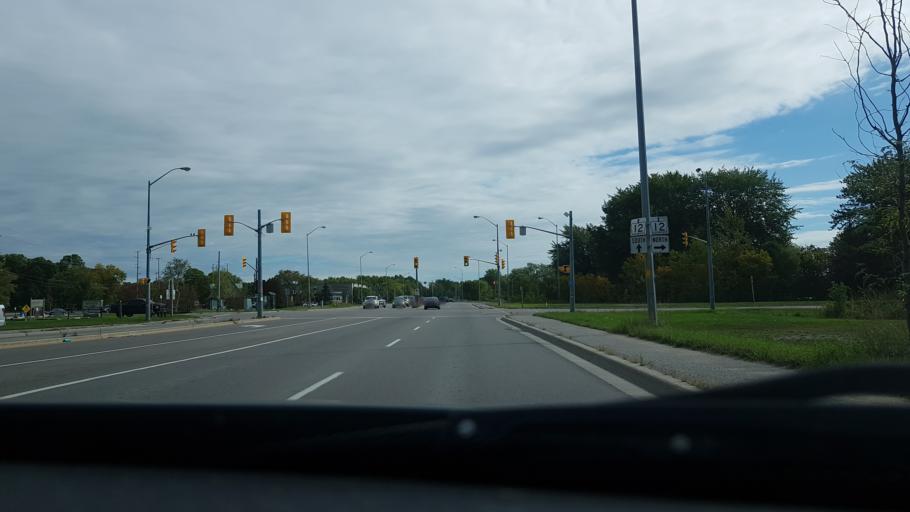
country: CA
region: Ontario
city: Orillia
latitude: 44.6060
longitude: -79.3886
